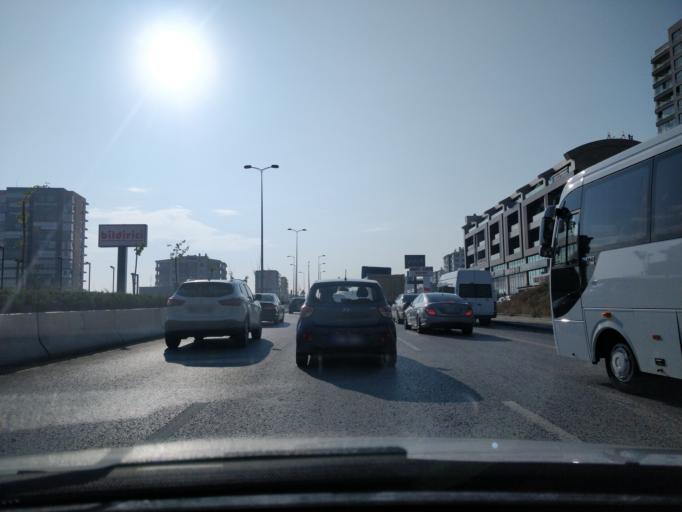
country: TR
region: Ankara
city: Etimesgut
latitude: 39.8975
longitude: 32.6503
